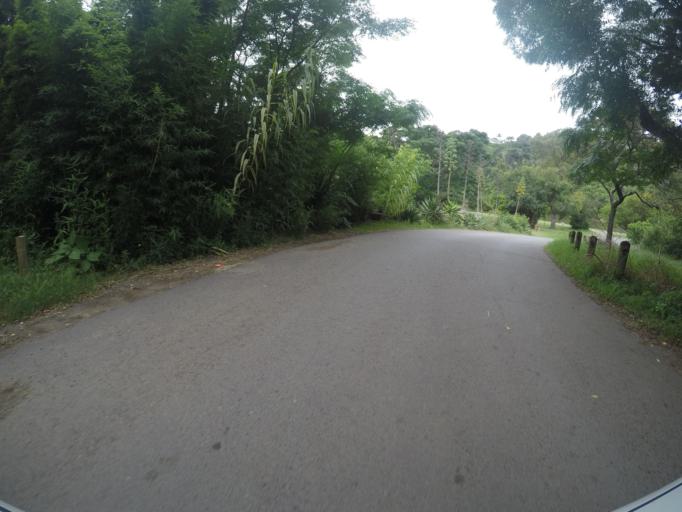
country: ZA
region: Eastern Cape
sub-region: Buffalo City Metropolitan Municipality
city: East London
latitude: -32.9745
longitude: 27.9274
